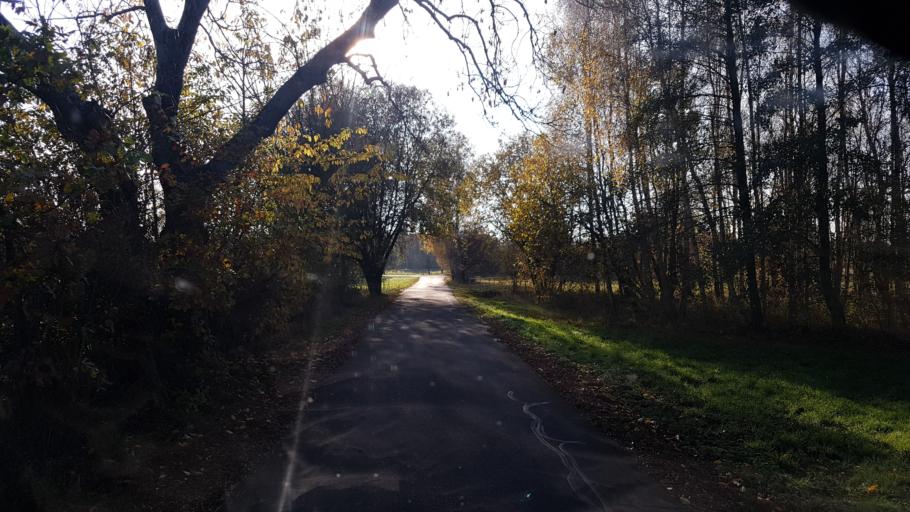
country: DE
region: Brandenburg
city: Schipkau
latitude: 51.5589
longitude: 13.8856
